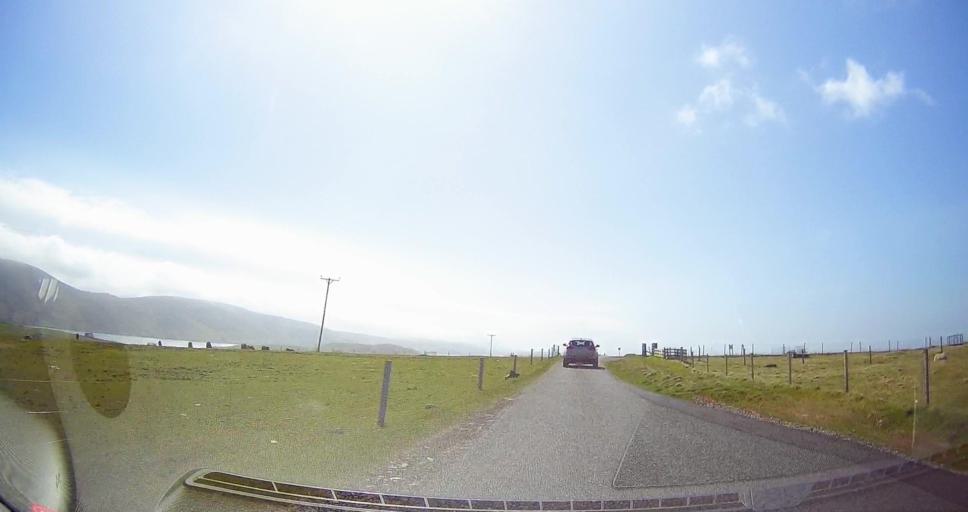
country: GB
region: Scotland
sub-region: Shetland Islands
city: Sandwick
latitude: 60.0753
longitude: -1.3383
